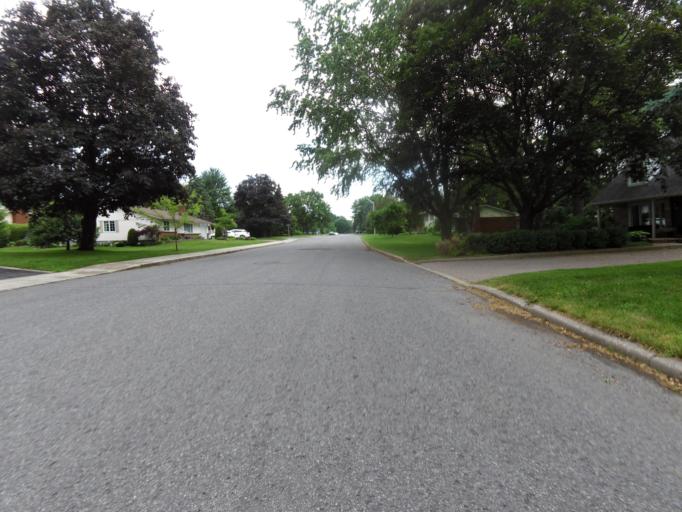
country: CA
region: Ontario
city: Bells Corners
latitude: 45.3401
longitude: -75.7767
